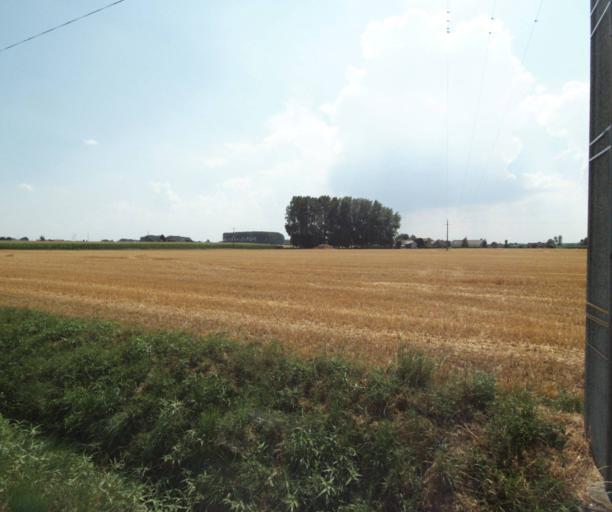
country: FR
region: Nord-Pas-de-Calais
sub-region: Departement du Nord
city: Deulemont
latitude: 50.7383
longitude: 2.9779
